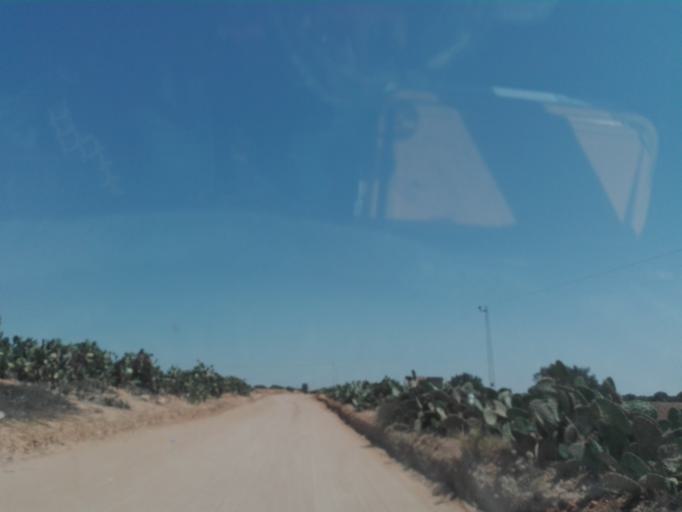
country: TN
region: Safaqis
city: Bi'r `Ali Bin Khalifah
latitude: 34.6656
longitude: 10.2382
